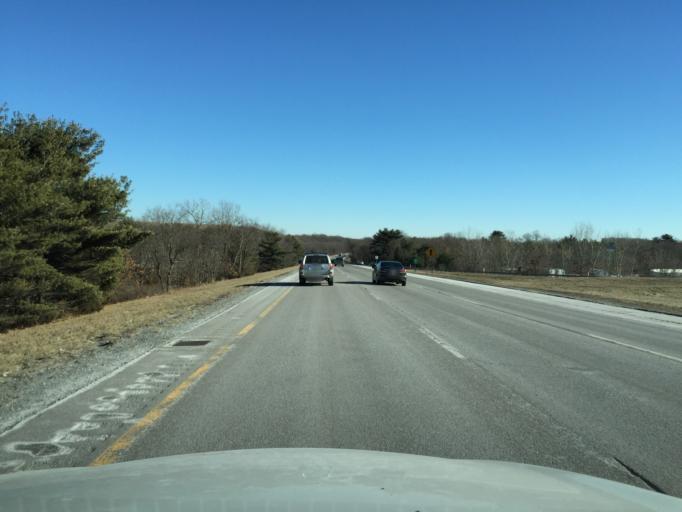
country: US
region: Massachusetts
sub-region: Norfolk County
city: Wrentham
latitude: 42.0370
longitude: -71.3050
